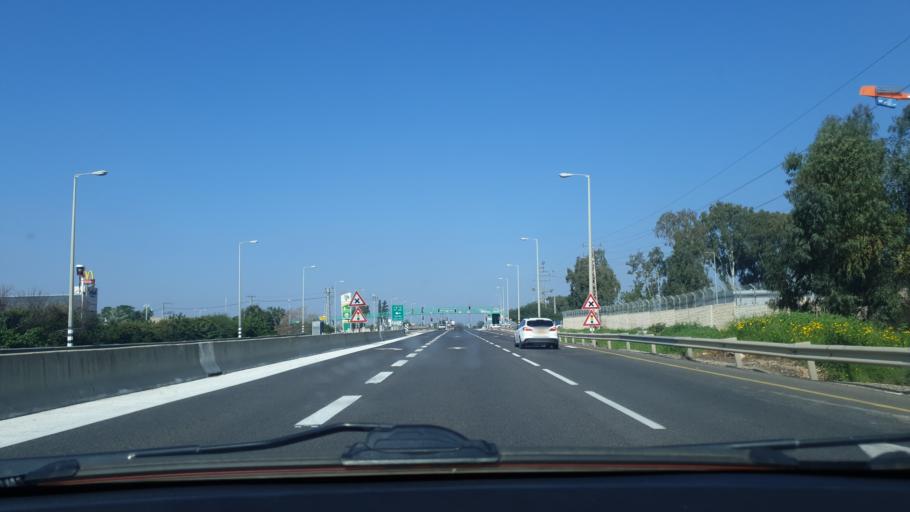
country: IL
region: Central District
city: Kefar Habad
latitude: 31.9678
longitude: 34.8453
